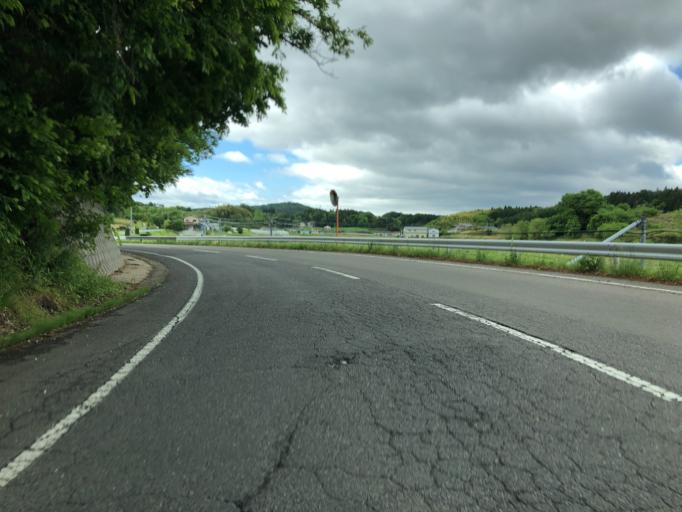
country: JP
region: Fukushima
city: Motomiya
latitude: 37.5147
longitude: 140.4736
